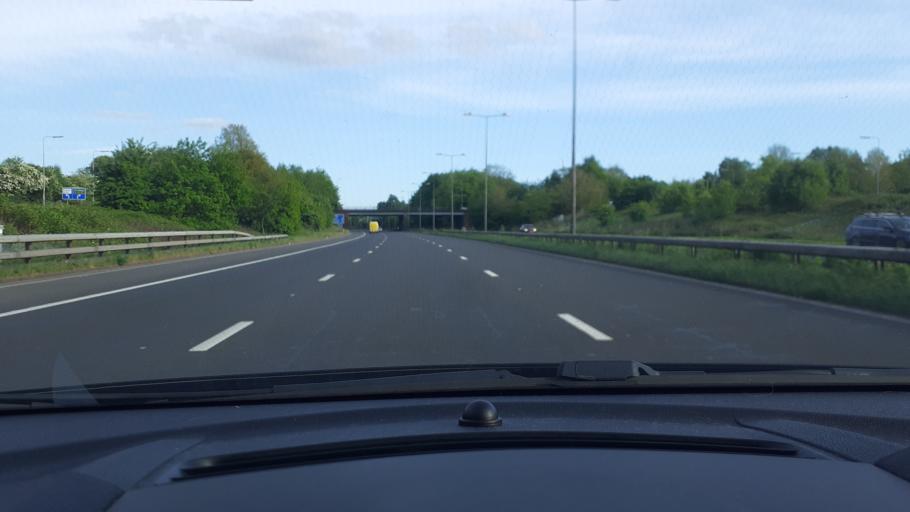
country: GB
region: England
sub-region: Borough of Wigan
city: Ashton in Makerfield
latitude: 53.4886
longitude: -2.6541
